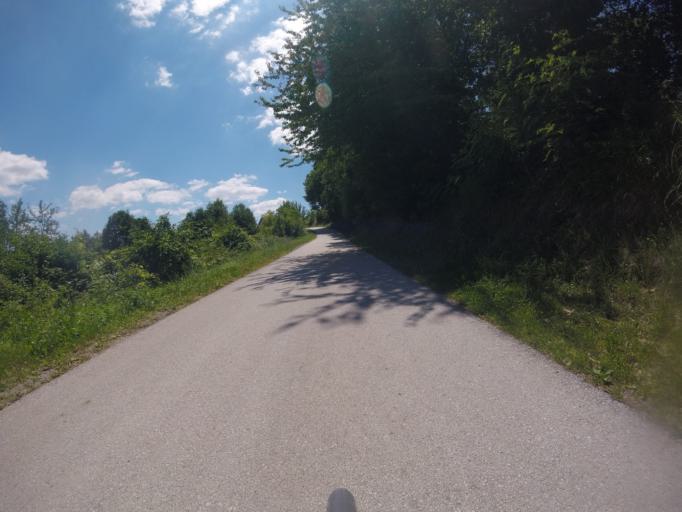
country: HR
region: Karlovacka
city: Ozalj
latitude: 45.6826
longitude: 15.4103
